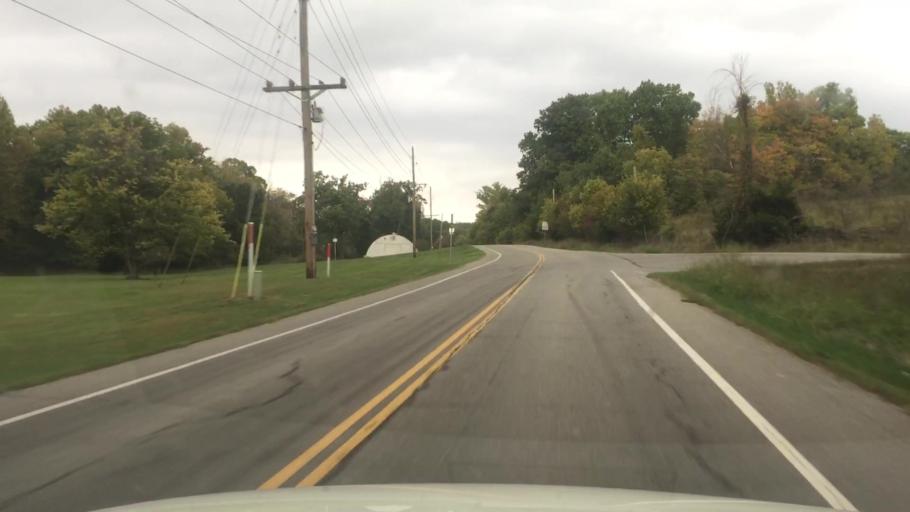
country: US
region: Missouri
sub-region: Boone County
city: Columbia
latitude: 38.8810
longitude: -92.4209
